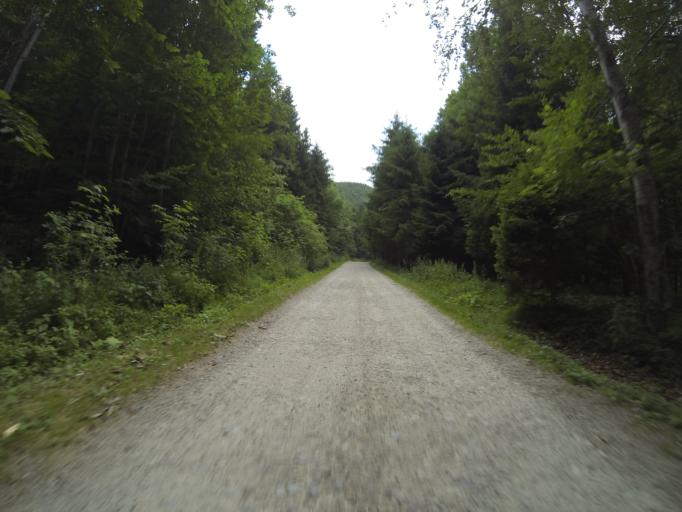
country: RO
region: Gorj
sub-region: Comuna Polovragi
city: Polovragi
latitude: 45.2654
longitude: 23.7712
